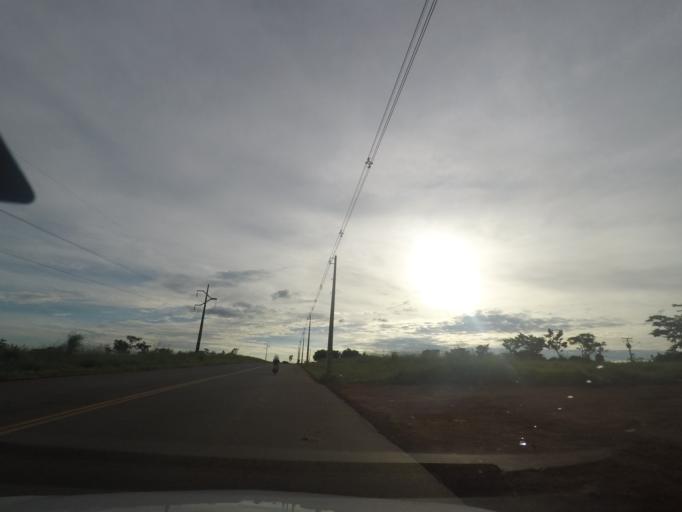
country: BR
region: Goias
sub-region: Trindade
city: Trindade
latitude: -16.7169
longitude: -49.3863
